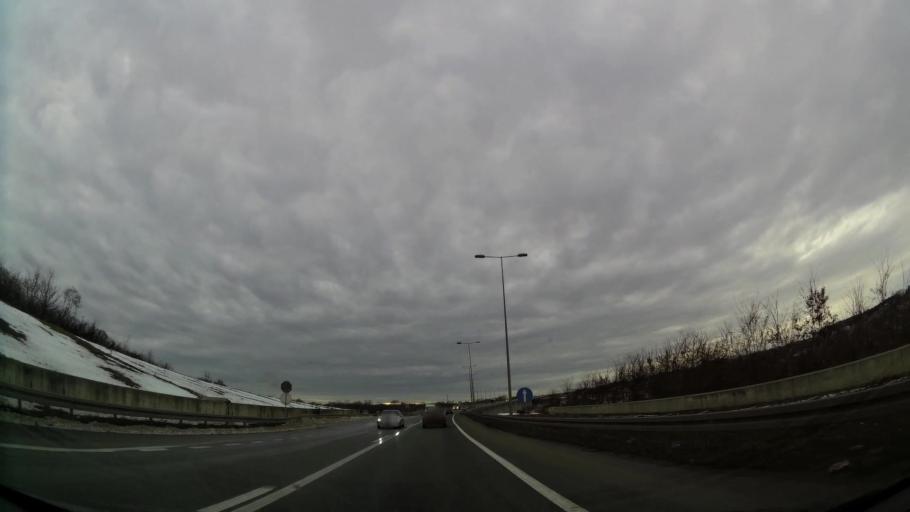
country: RS
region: Central Serbia
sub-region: Belgrade
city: Rakovica
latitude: 44.7132
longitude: 20.4289
